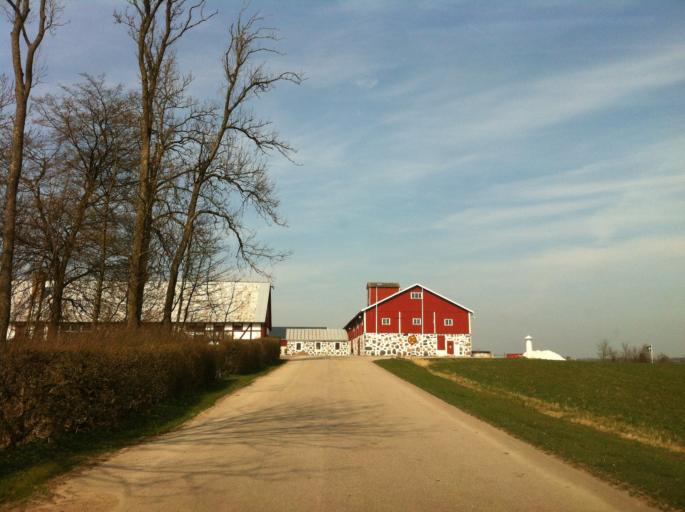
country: SE
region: Skane
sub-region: Svalovs Kommun
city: Svaloev
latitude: 55.9247
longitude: 13.1021
